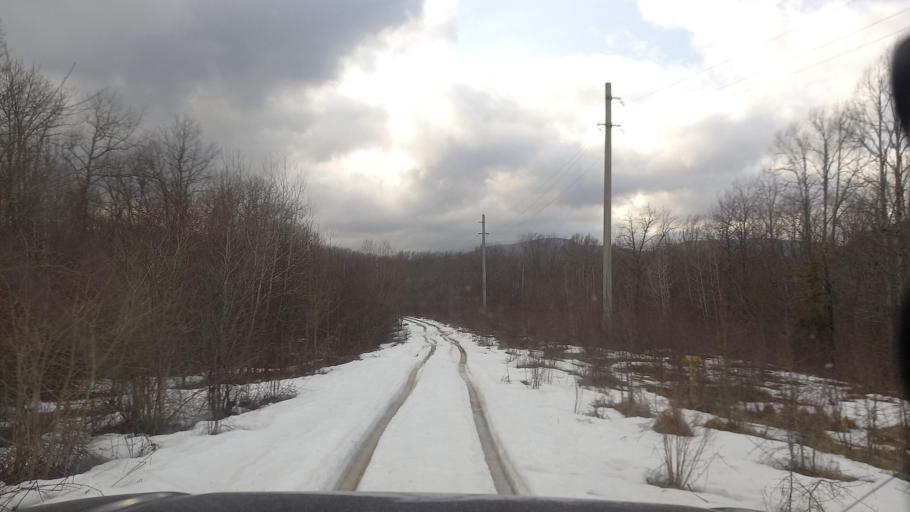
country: RU
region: Krasnodarskiy
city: Smolenskaya
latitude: 44.5719
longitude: 38.7975
